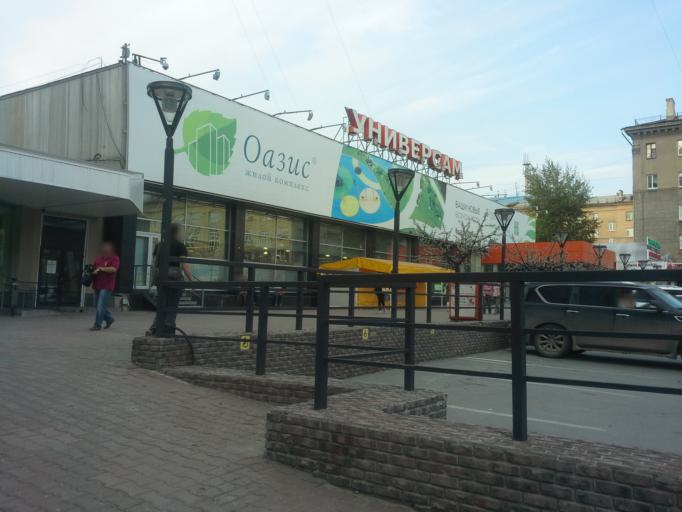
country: RU
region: Novosibirsk
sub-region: Novosibirskiy Rayon
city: Novosibirsk
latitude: 55.0296
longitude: 82.9138
